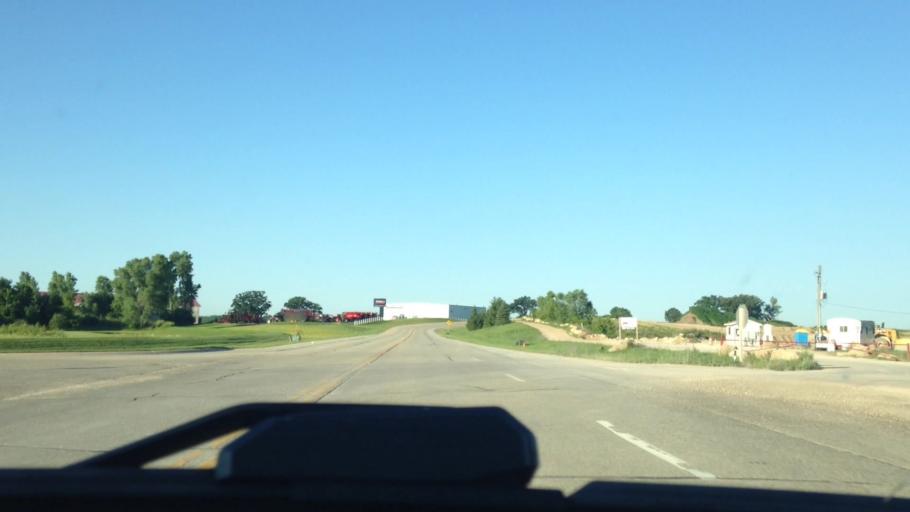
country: US
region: Wisconsin
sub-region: Columbia County
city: Columbus
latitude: 43.3460
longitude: -89.0444
